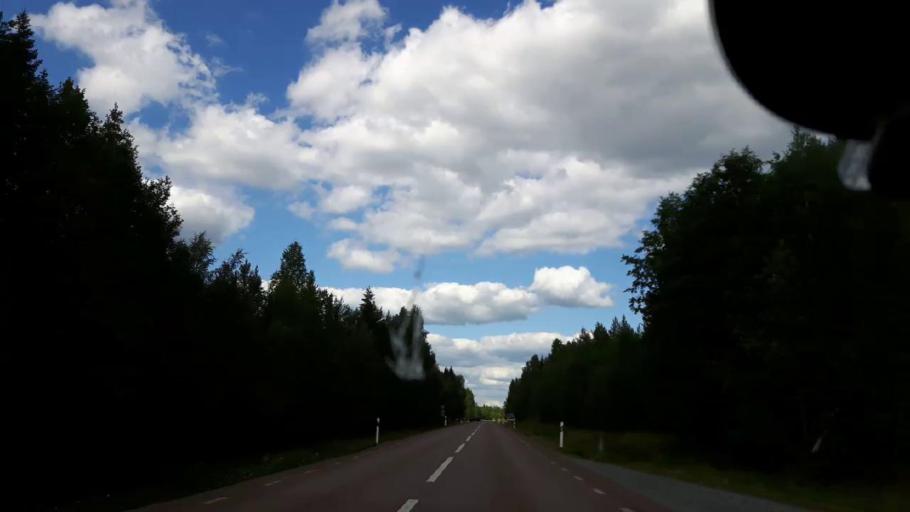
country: SE
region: Jaemtland
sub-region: Ragunda Kommun
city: Hammarstrand
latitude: 62.9264
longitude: 16.6998
